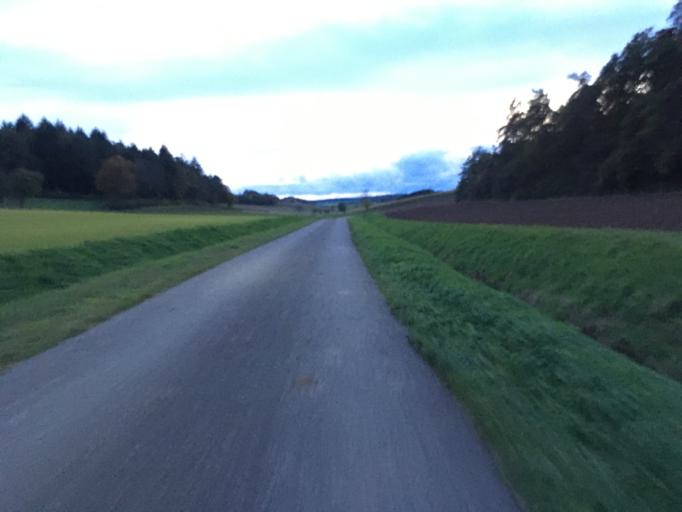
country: DE
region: Baden-Wuerttemberg
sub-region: Karlsruhe Region
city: Osterburken
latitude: 49.3788
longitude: 9.4453
